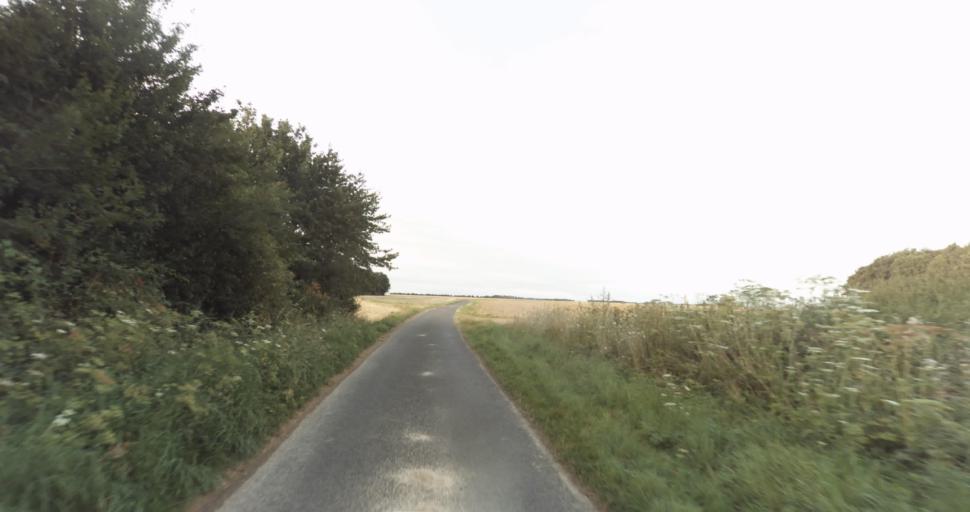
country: FR
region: Haute-Normandie
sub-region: Departement de l'Eure
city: La Madeleine-de-Nonancourt
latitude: 48.8610
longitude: 1.2220
